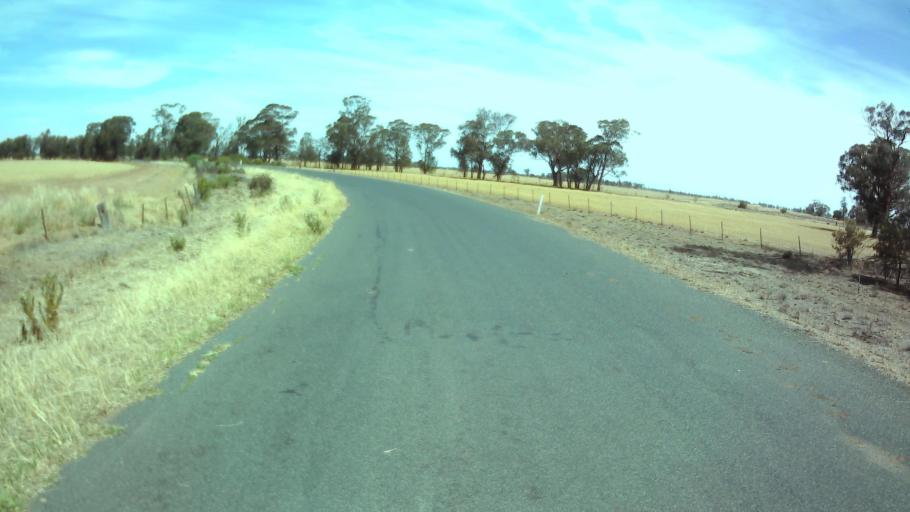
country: AU
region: New South Wales
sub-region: Weddin
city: Grenfell
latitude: -33.9554
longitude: 147.7771
